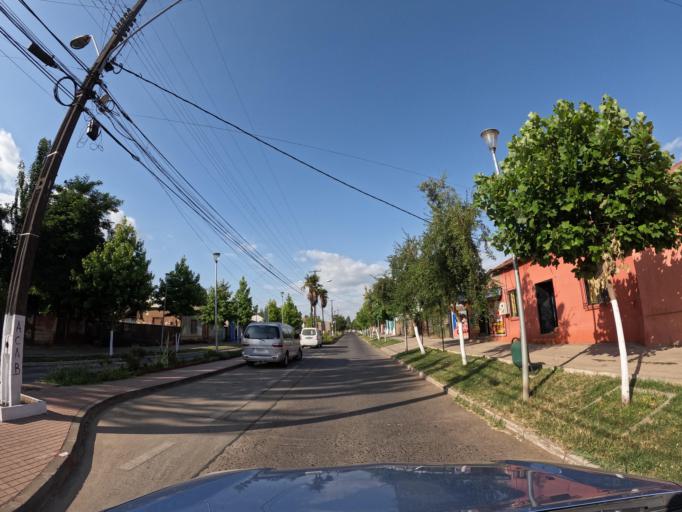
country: CL
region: Maule
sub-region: Provincia de Curico
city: Molina
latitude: -35.2863
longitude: -71.2613
